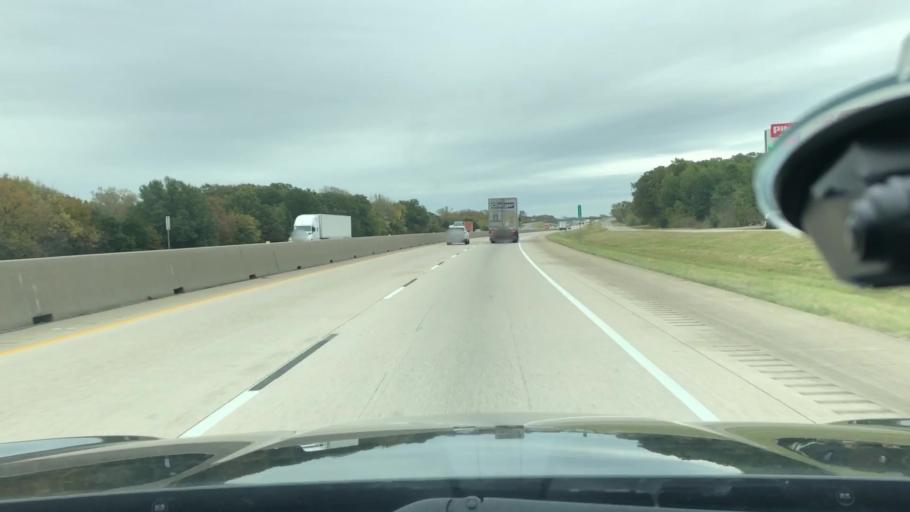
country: US
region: Texas
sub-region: Hopkins County
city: Sulphur Springs
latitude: 33.1264
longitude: -95.7434
